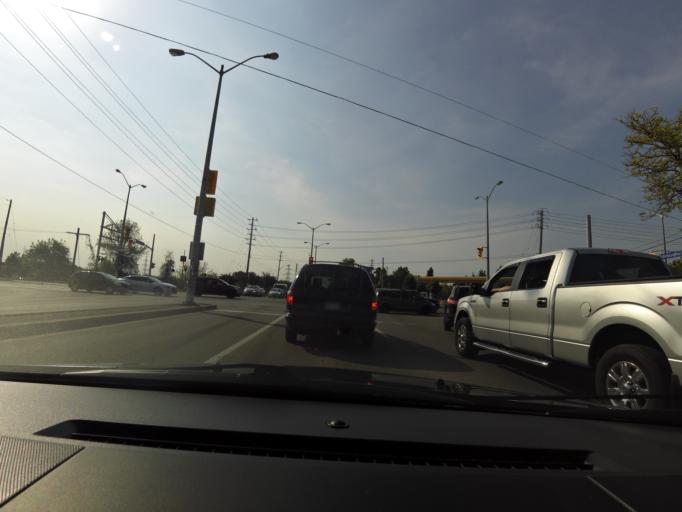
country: CA
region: Ontario
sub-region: Wellington County
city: Guelph
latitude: 43.5514
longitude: -80.2774
